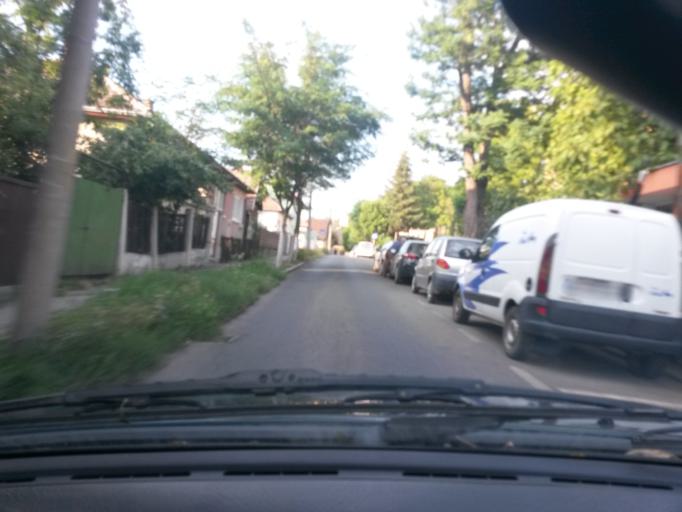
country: RO
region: Mures
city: Targu-Mures
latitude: 46.5461
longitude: 24.5717
